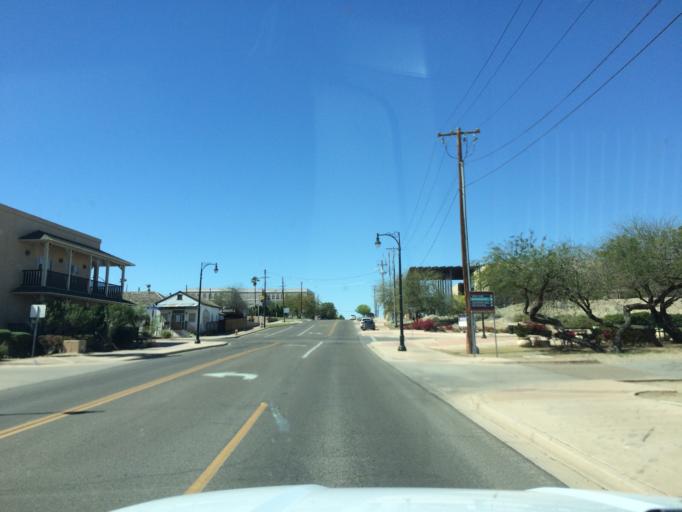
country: US
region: Arizona
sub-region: Yuma County
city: Yuma
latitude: 32.7253
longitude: -114.6190
